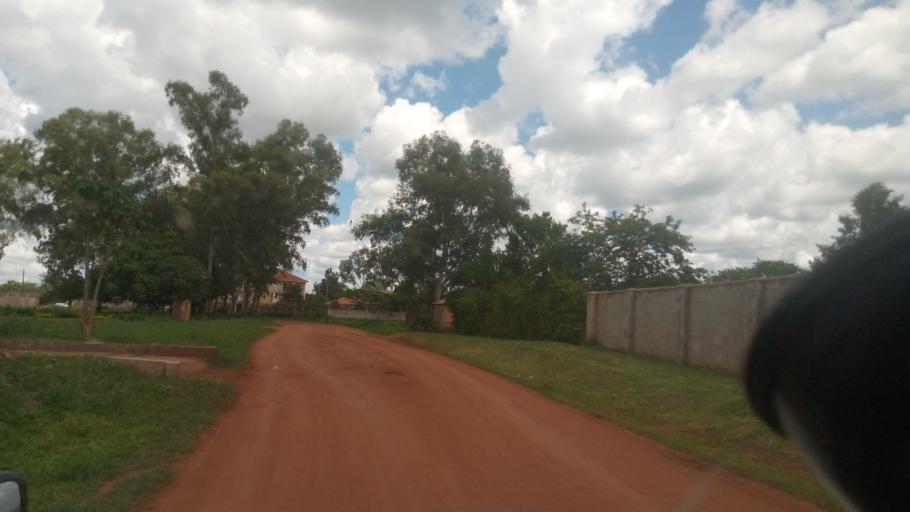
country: UG
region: Northern Region
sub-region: Lira District
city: Lira
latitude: 2.2392
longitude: 32.9048
